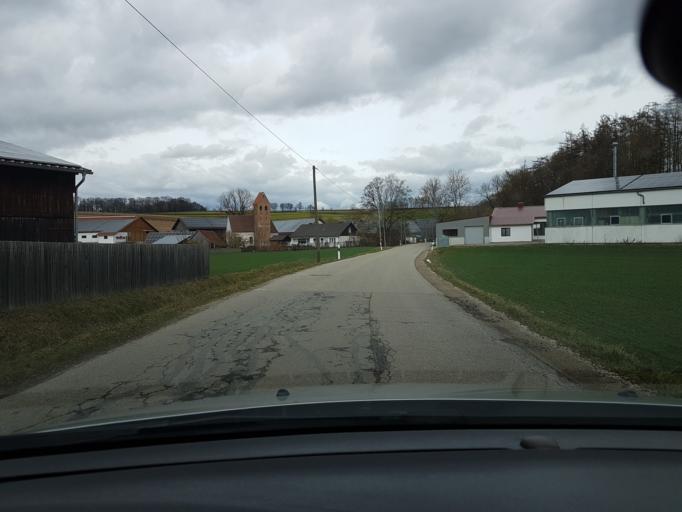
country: DE
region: Bavaria
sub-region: Lower Bavaria
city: Landshut
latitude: 48.5180
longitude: 12.1755
